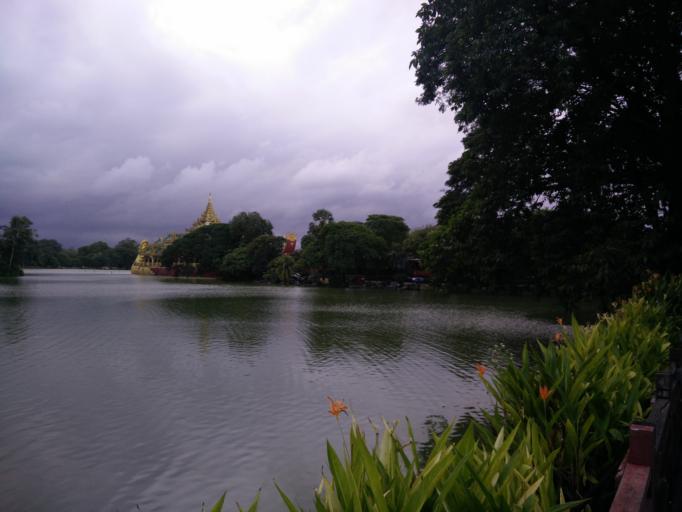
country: MM
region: Yangon
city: Yangon
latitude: 16.7937
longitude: 96.1698
